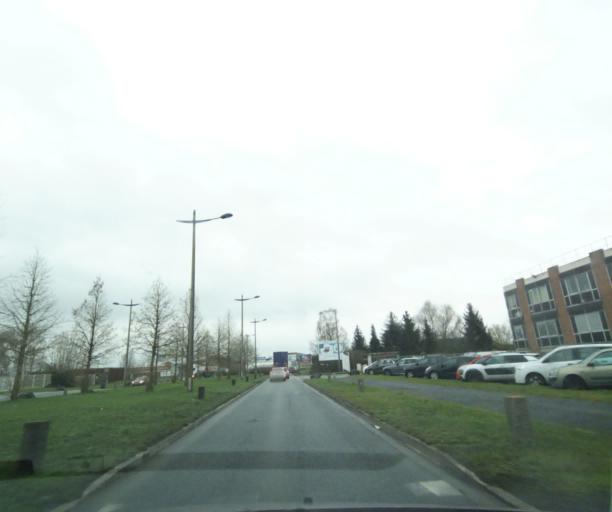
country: FR
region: Nord-Pas-de-Calais
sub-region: Departement du Nord
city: Prouvy
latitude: 50.3325
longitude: 3.4578
